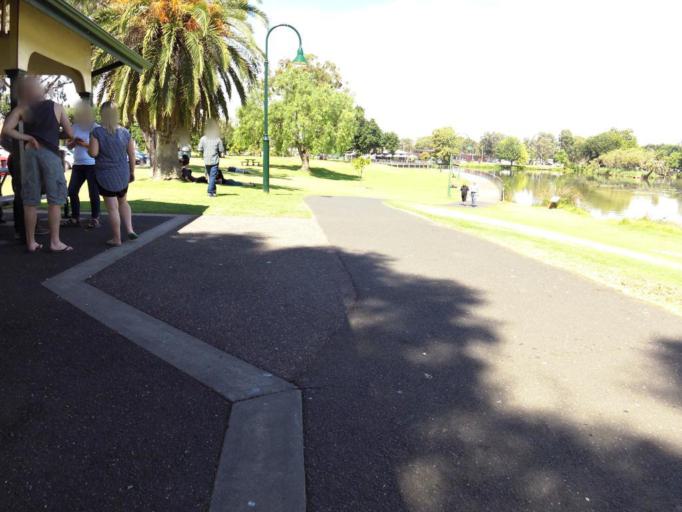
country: AU
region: Victoria
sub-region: Greater Bendigo
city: Bendigo
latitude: -36.7476
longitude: 144.2918
